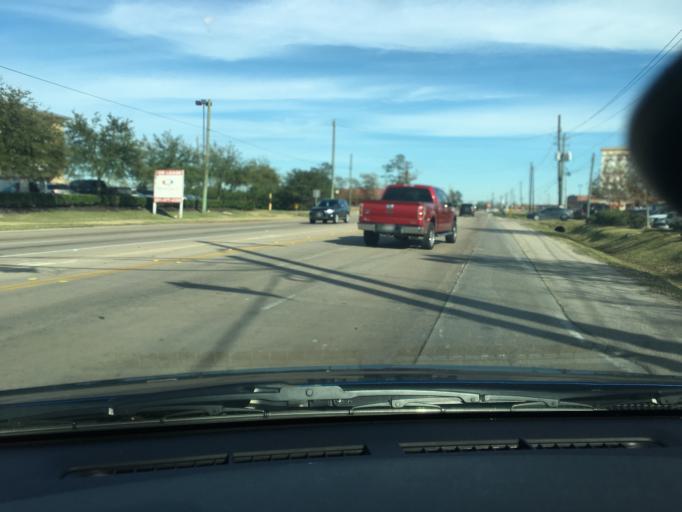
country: US
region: Texas
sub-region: Harris County
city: Cloverleaf
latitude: 29.8096
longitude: -95.1599
